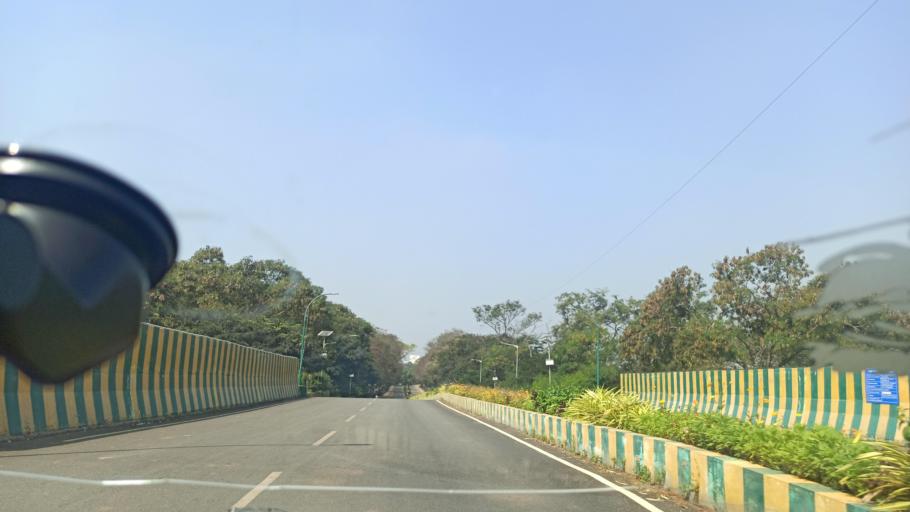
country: IN
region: Karnataka
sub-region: Bangalore Urban
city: Yelahanka
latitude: 13.0738
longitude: 77.5894
